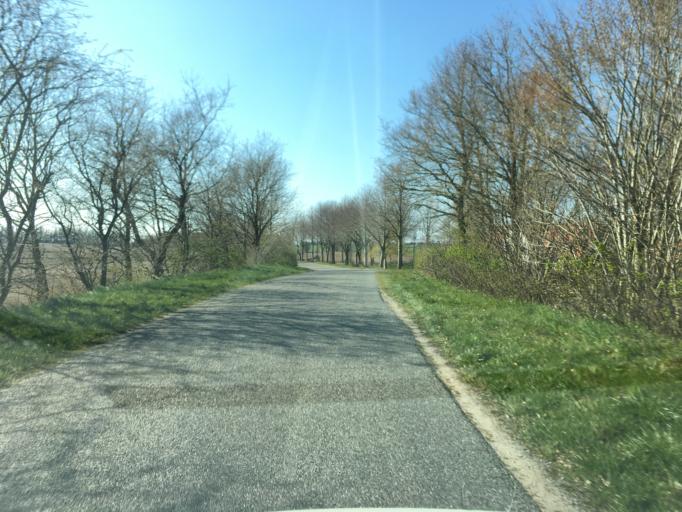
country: DK
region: South Denmark
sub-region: Aabenraa Kommune
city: Krusa
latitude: 54.9273
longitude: 9.4210
